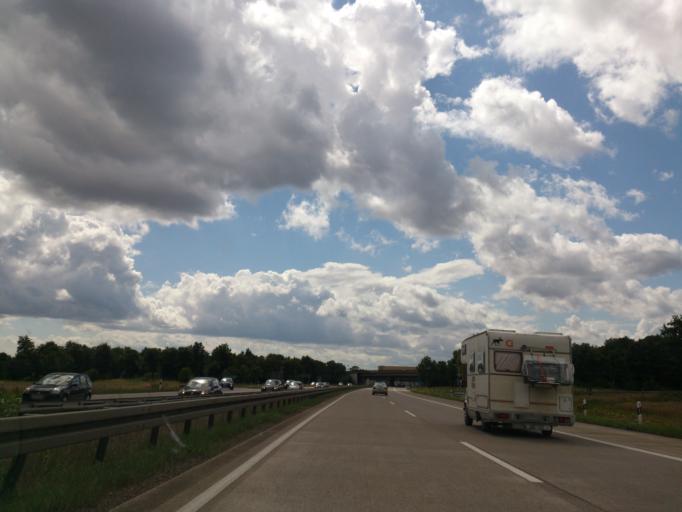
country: DE
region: Lower Saxony
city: Langenhagen
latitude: 52.4616
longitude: 9.7226
